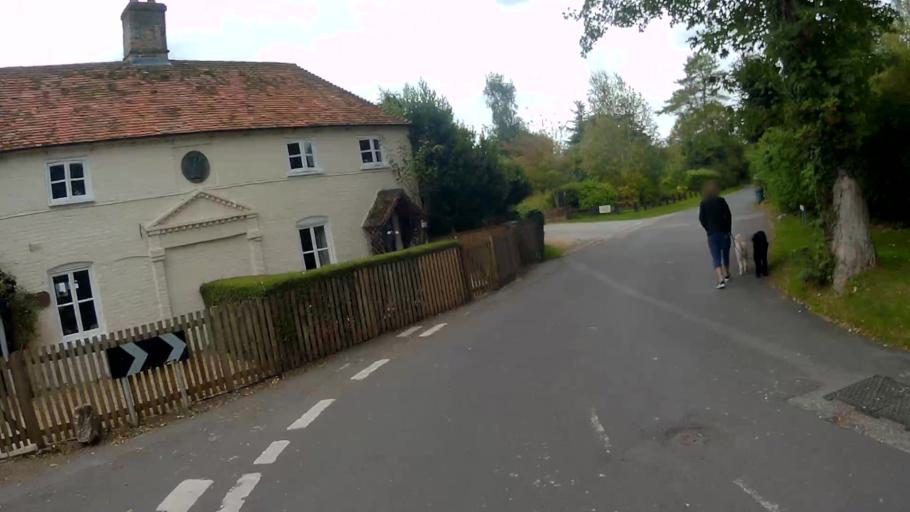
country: GB
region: England
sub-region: Hampshire
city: Basingstoke
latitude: 51.2106
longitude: -1.1593
